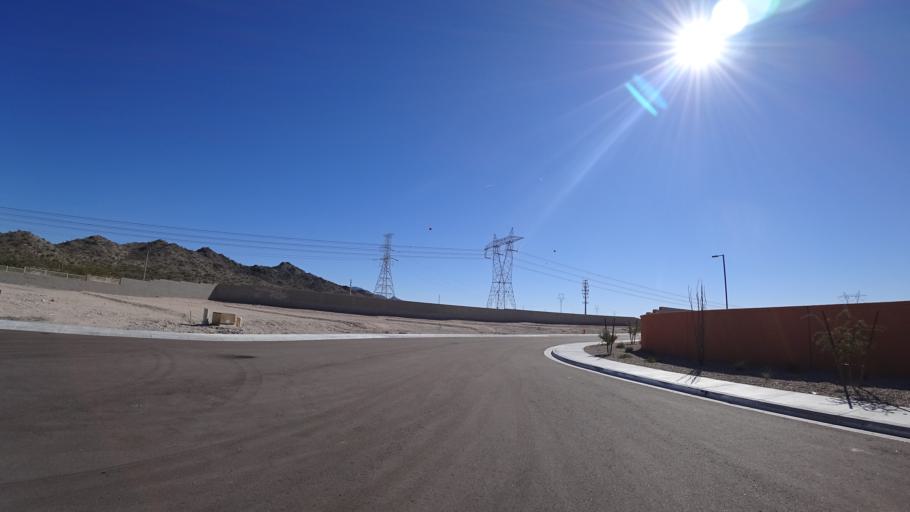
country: US
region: Arizona
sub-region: Maricopa County
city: Goodyear
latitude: 33.3487
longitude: -112.4241
